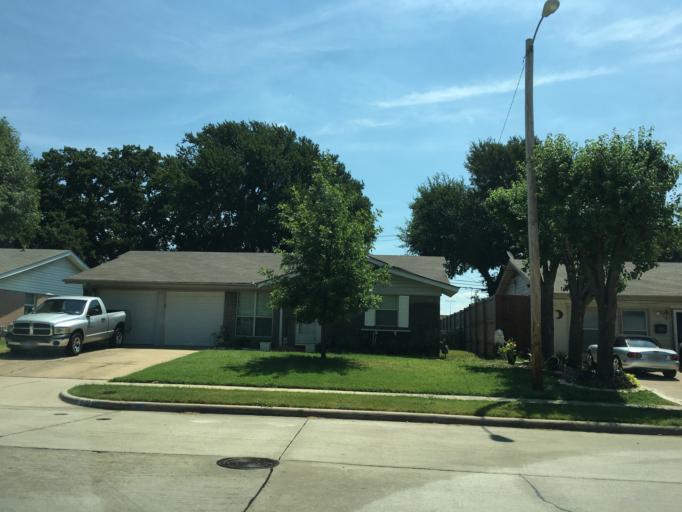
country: US
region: Texas
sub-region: Denton County
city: Lewisville
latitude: 33.0296
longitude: -96.9975
